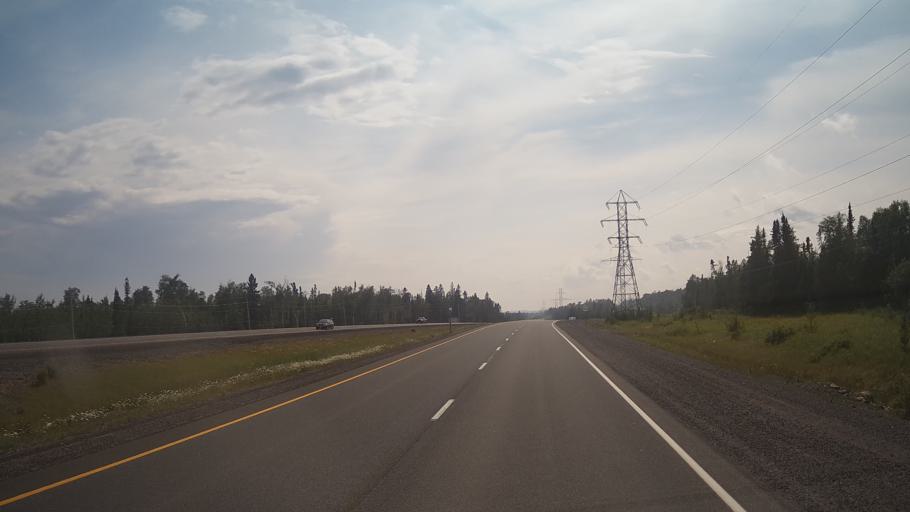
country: CA
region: Ontario
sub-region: Thunder Bay District
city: Thunder Bay
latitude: 48.5704
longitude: -88.8331
